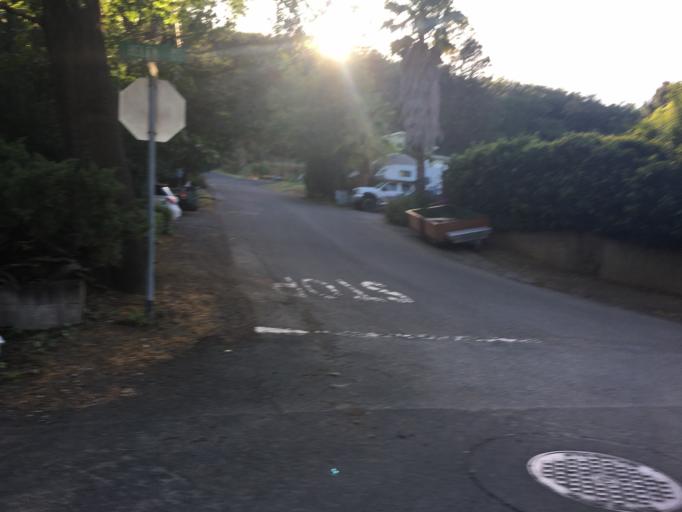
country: US
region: California
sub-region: Mendocino County
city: Ukiah
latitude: 39.1319
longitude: -123.2137
